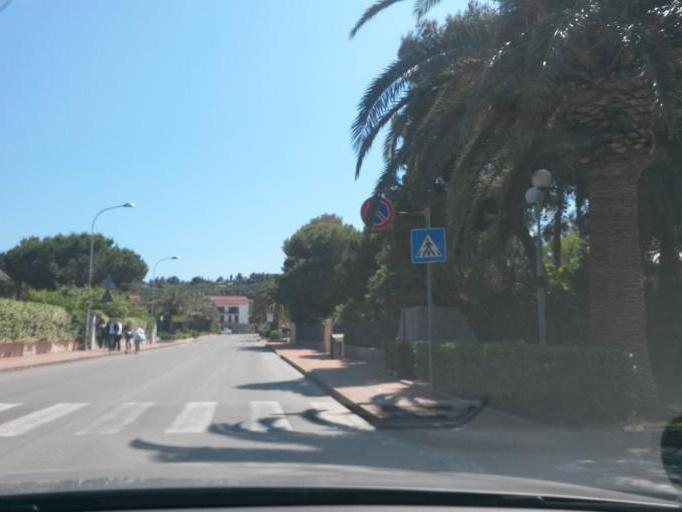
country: IT
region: Tuscany
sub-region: Provincia di Livorno
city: Campo nell'Elba
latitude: 42.7454
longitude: 10.2323
